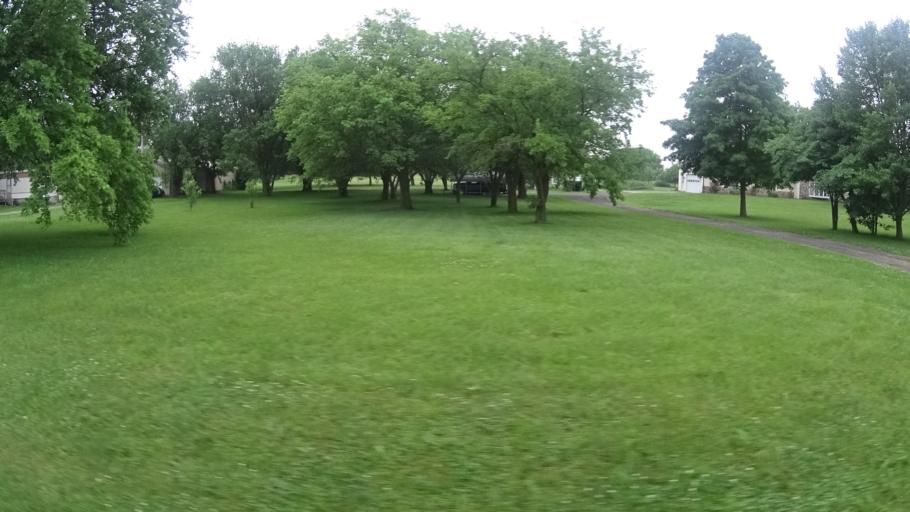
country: US
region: Ohio
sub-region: Huron County
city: Bellevue
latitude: 41.3506
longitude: -82.8225
